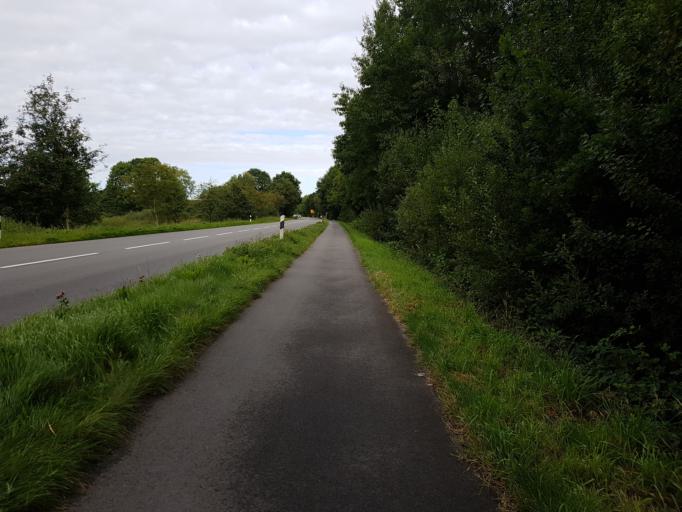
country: DE
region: Lower Saxony
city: Wittmund
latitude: 53.5700
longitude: 7.7696
